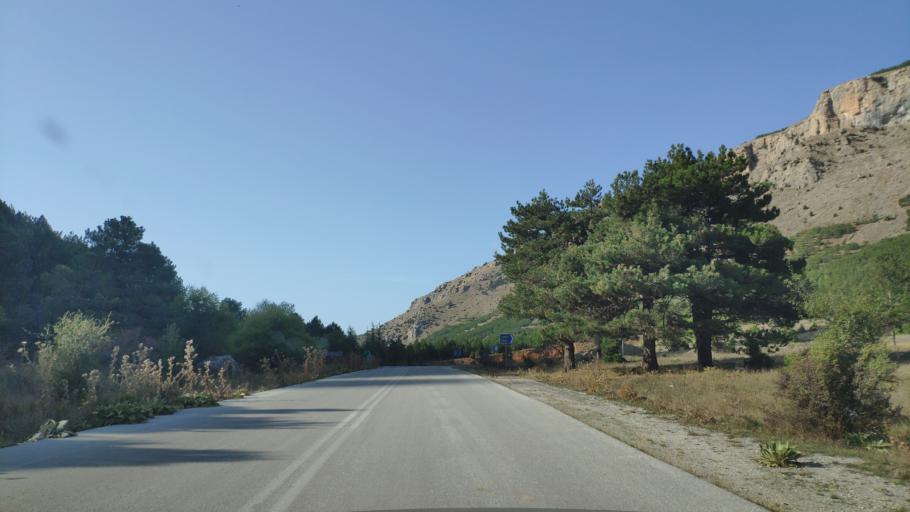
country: GR
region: West Greece
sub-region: Nomos Achaias
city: Aiyira
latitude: 38.0353
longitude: 22.4000
